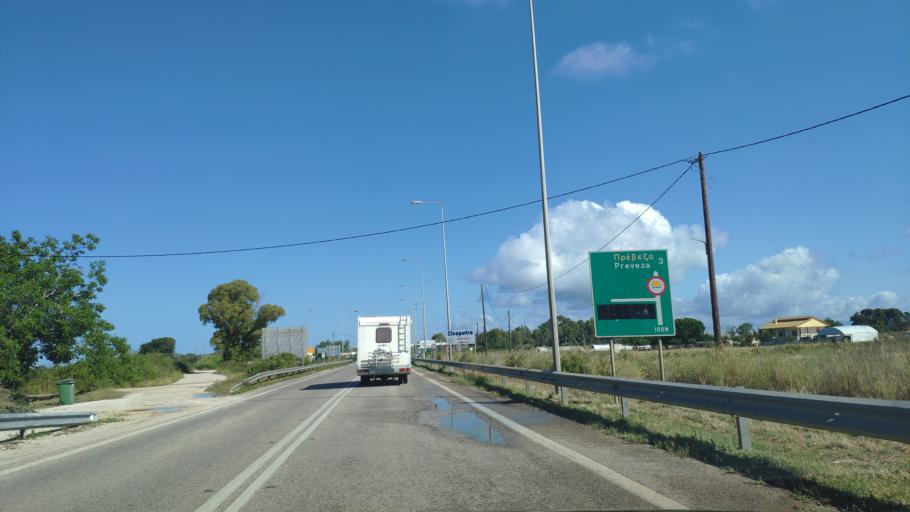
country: GR
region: Epirus
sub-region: Nomos Prevezis
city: Preveza
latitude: 38.9365
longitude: 20.7690
